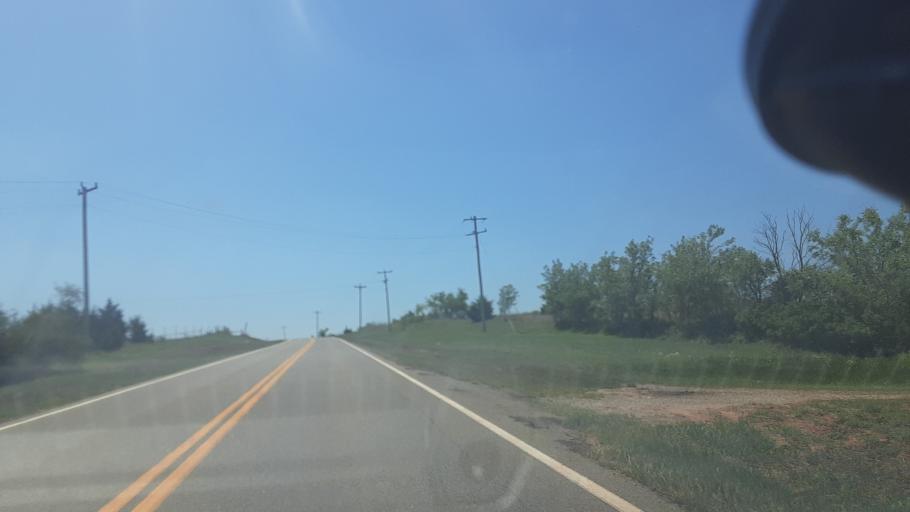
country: US
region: Oklahoma
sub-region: Logan County
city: Guthrie
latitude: 36.0444
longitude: -97.4075
